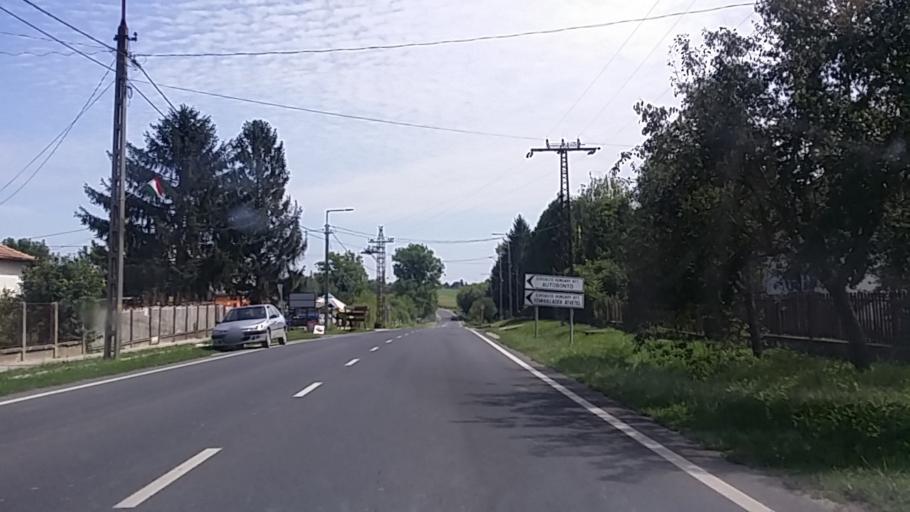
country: HU
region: Somogy
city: Taszar
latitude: 46.3646
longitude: 18.0111
